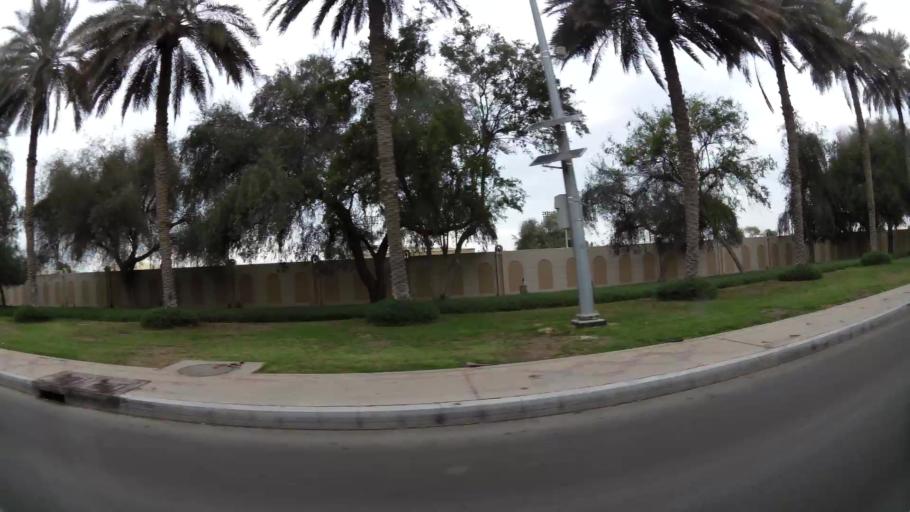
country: AE
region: Abu Dhabi
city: Abu Dhabi
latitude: 24.4392
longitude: 54.3819
